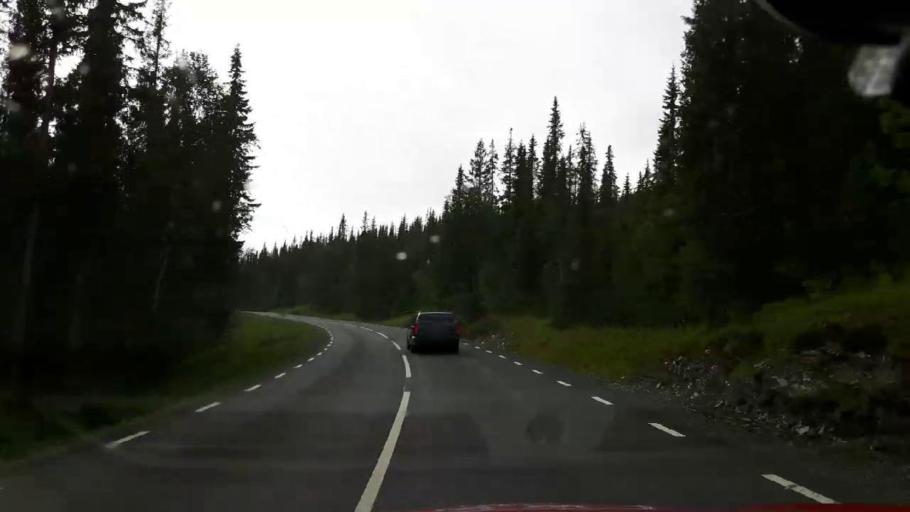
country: NO
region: Nord-Trondelag
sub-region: Royrvik
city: Royrvik
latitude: 64.8604
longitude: 14.1812
